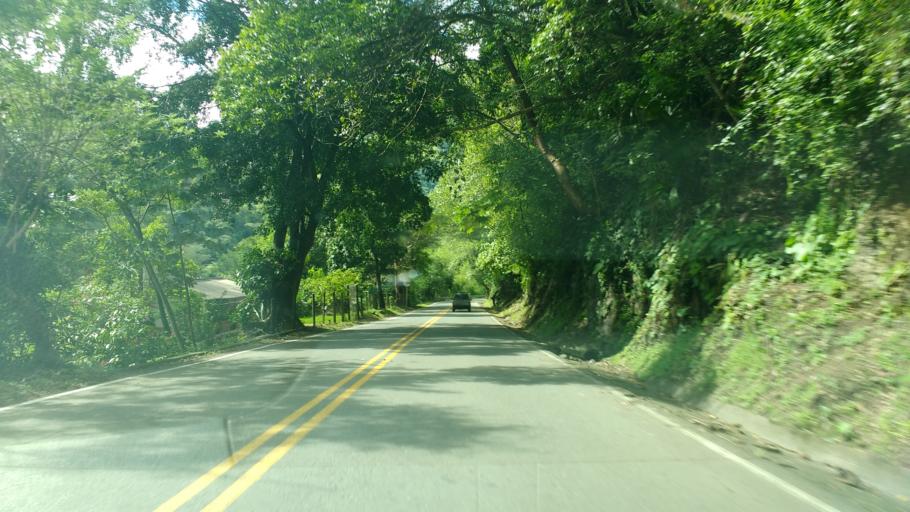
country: CO
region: Antioquia
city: Titiribi
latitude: 6.0008
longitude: -75.7902
